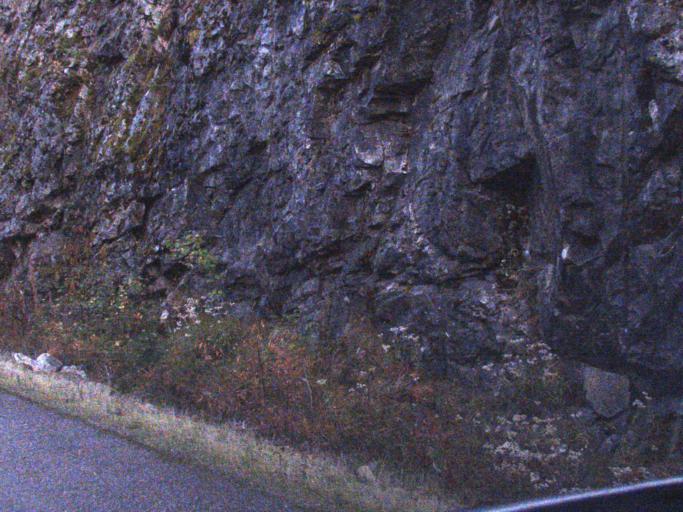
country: US
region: Washington
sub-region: Snohomish County
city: Darrington
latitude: 48.7047
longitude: -120.9526
